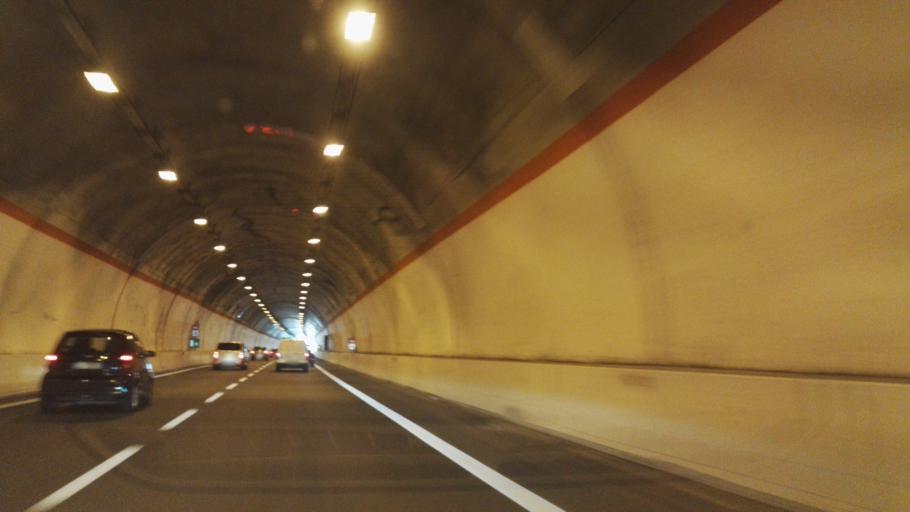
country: IT
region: Calabria
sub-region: Provincia di Catanzaro
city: Roccelletta
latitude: 38.8176
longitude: 16.5607
